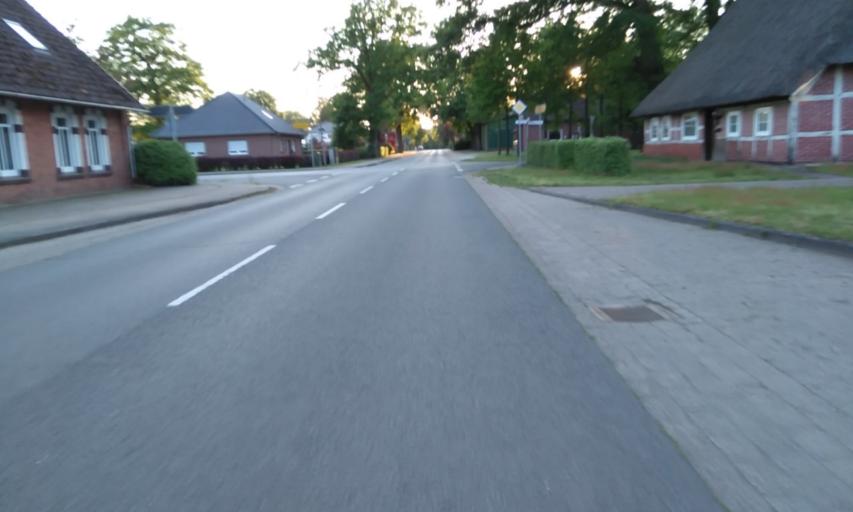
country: DE
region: Lower Saxony
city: Ahlerstedt
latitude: 53.4259
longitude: 9.4290
